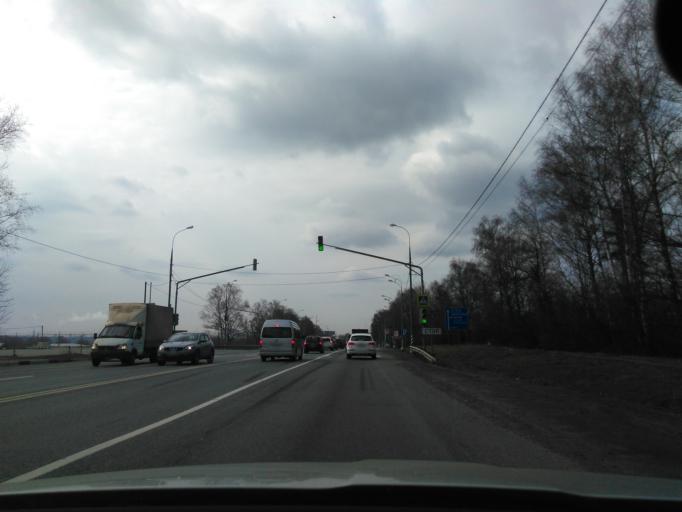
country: RU
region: Moskovskaya
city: Sheremet'yevskiy
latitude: 55.9984
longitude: 37.5365
